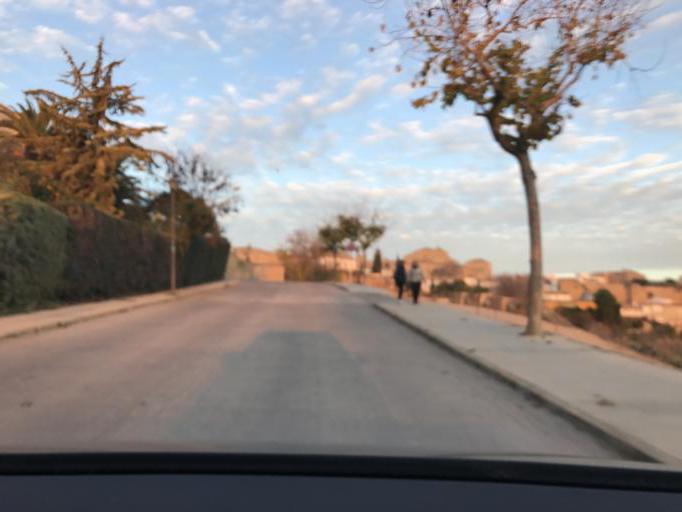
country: ES
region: Andalusia
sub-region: Provincia de Jaen
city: Ubeda
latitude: 38.0060
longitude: -3.3719
